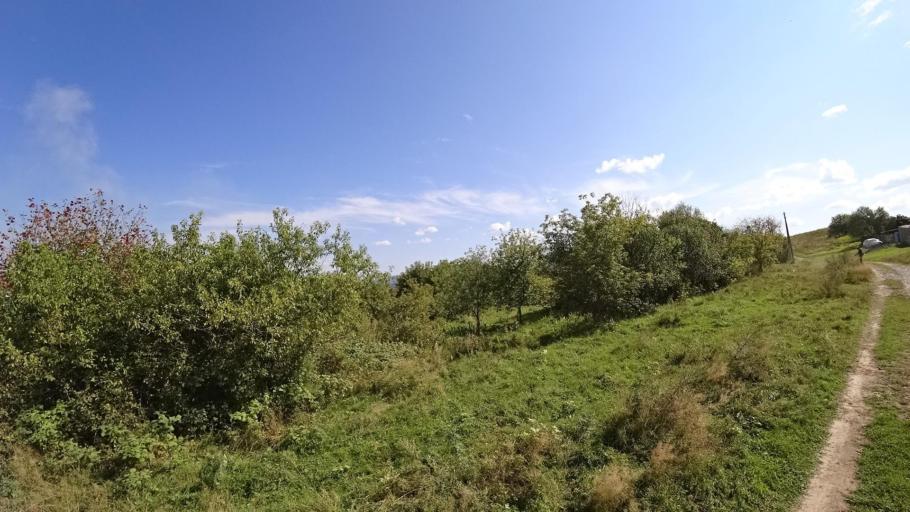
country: RU
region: Jewish Autonomous Oblast
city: Londoko
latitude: 49.0098
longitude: 131.8660
